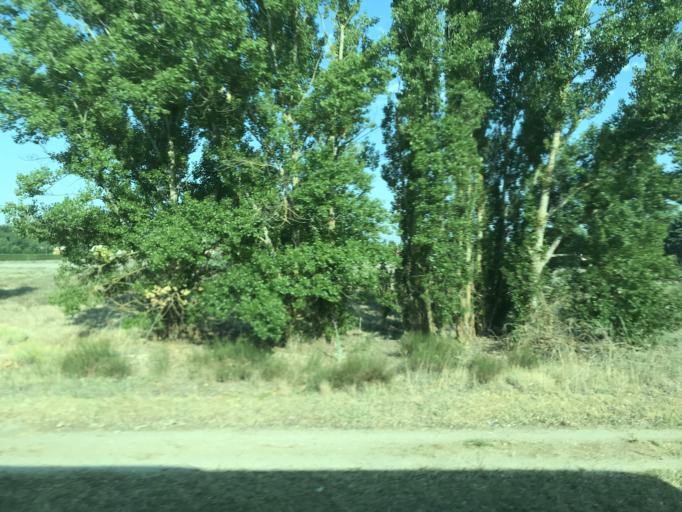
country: ES
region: Castille and Leon
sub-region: Provincia de Valladolid
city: Mojados
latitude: 41.4437
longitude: -4.6646
